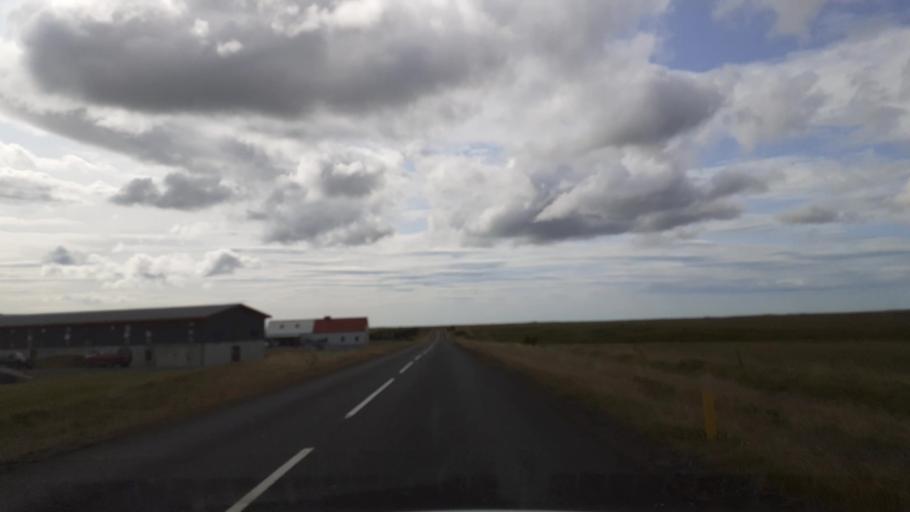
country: IS
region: South
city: Vestmannaeyjar
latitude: 63.8323
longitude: -20.4218
